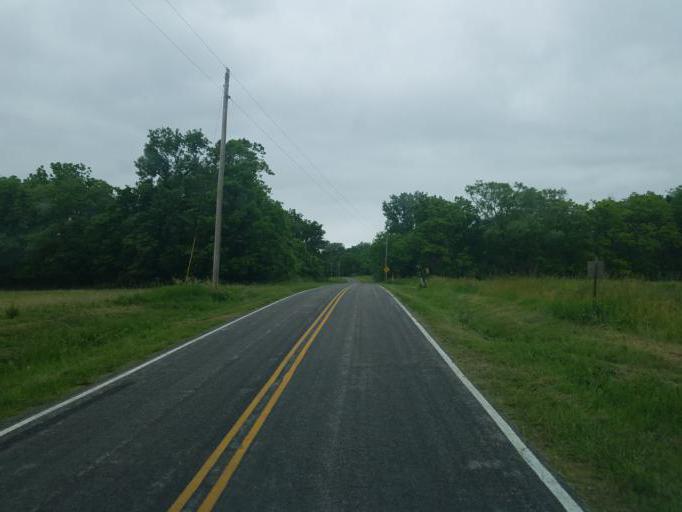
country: US
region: Ohio
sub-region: Marion County
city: Marion
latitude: 40.5472
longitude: -83.0192
